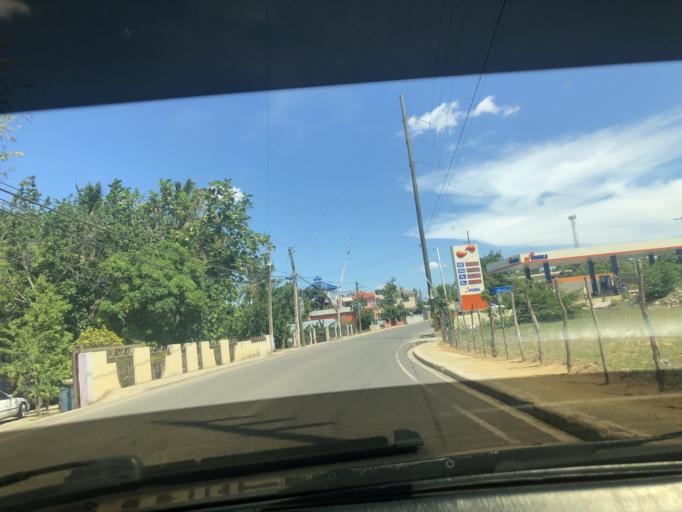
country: DO
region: Santiago
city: Santiago de los Caballeros
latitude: 19.4022
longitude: -70.6704
